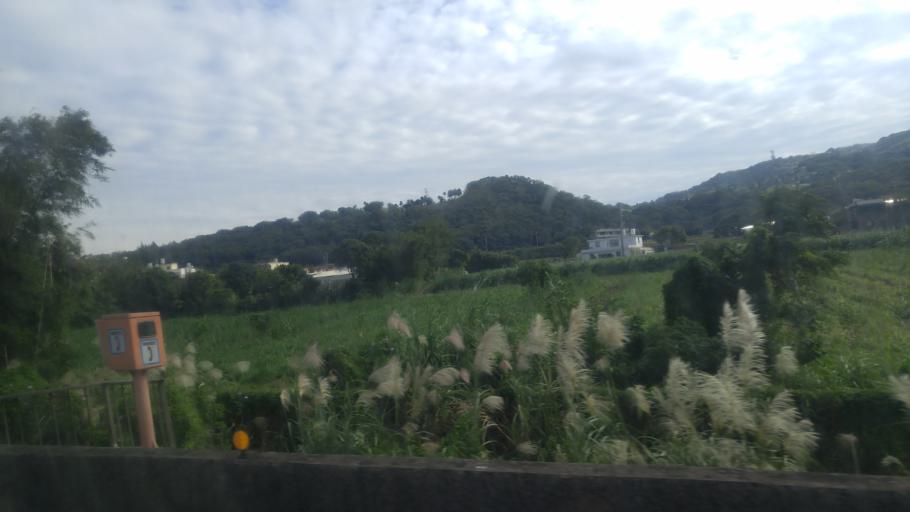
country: TW
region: Taiwan
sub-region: Hsinchu
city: Zhubei
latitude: 24.8930
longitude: 121.1214
